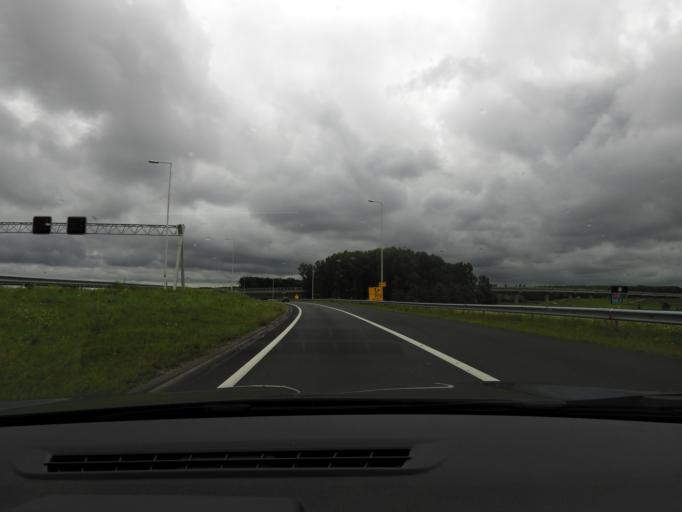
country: NL
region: South Holland
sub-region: Gemeente Albrandswaard
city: Rhoon
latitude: 51.8723
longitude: 4.3816
